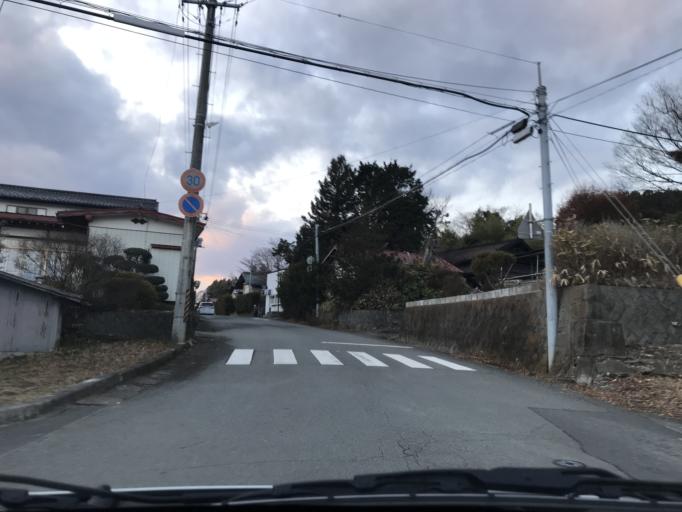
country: JP
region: Iwate
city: Ichinoseki
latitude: 38.8020
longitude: 141.1214
